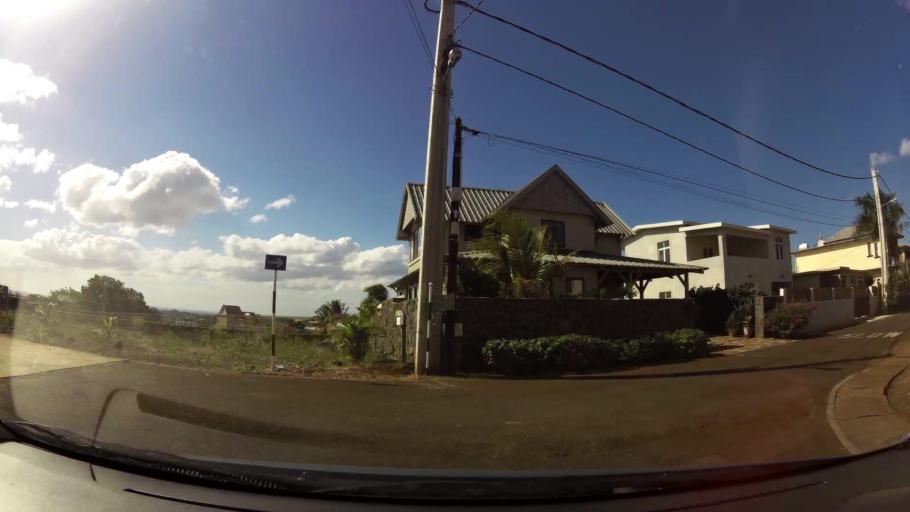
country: MU
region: Black River
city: Albion
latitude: -20.2218
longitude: 57.4139
